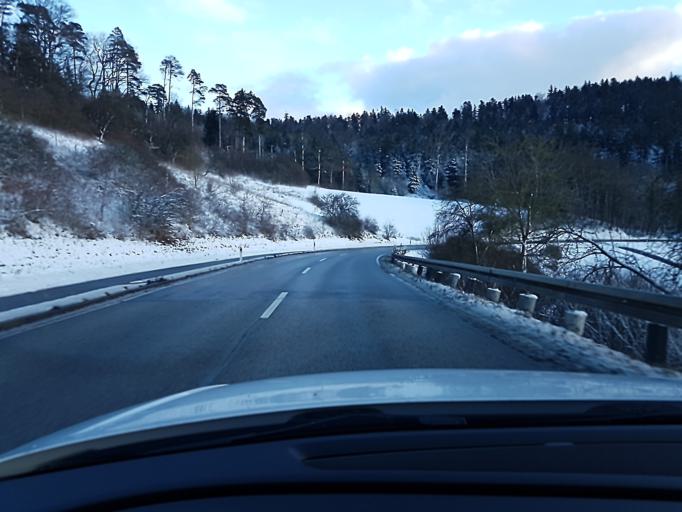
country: DE
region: Baden-Wuerttemberg
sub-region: Regierungsbezirk Stuttgart
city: Fichtenberg
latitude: 48.9835
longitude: 9.6808
